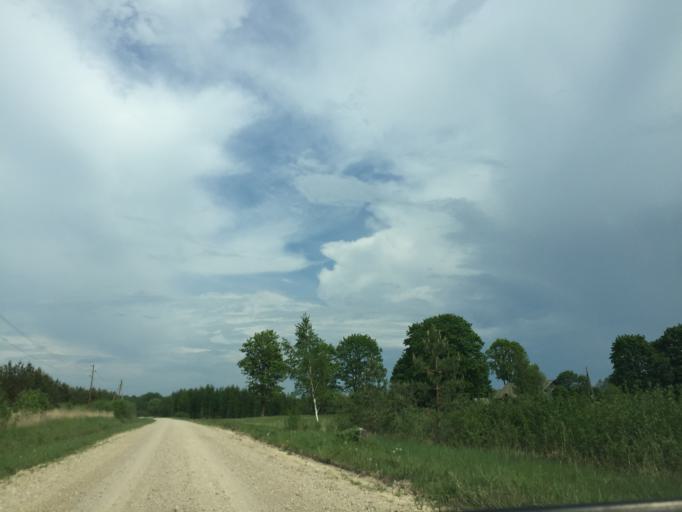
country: LV
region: Livani
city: Livani
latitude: 56.5850
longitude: 26.1928
